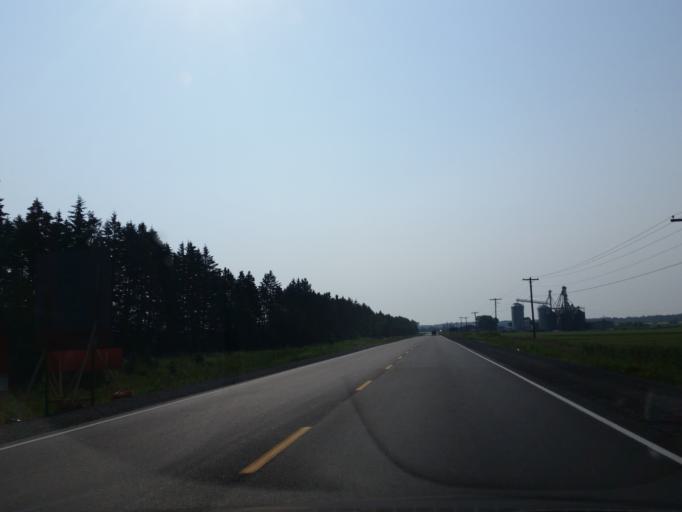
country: CA
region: Ontario
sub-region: Nipissing District
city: North Bay
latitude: 46.4101
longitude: -80.1116
